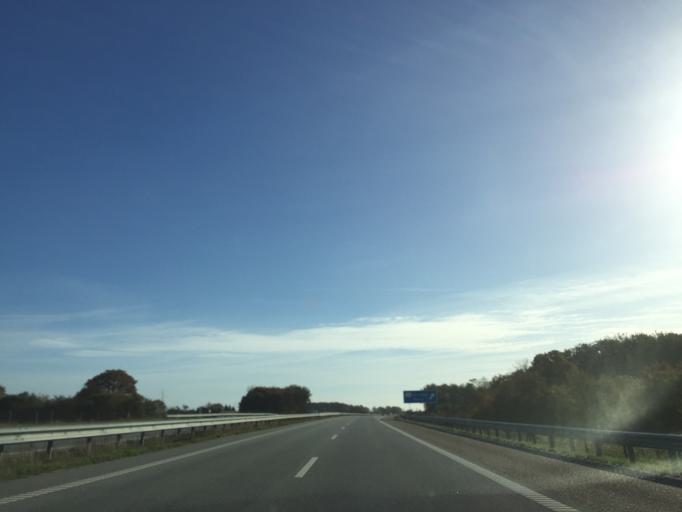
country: DK
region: South Denmark
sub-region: Sonderborg Kommune
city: Grasten
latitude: 54.9549
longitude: 9.6283
